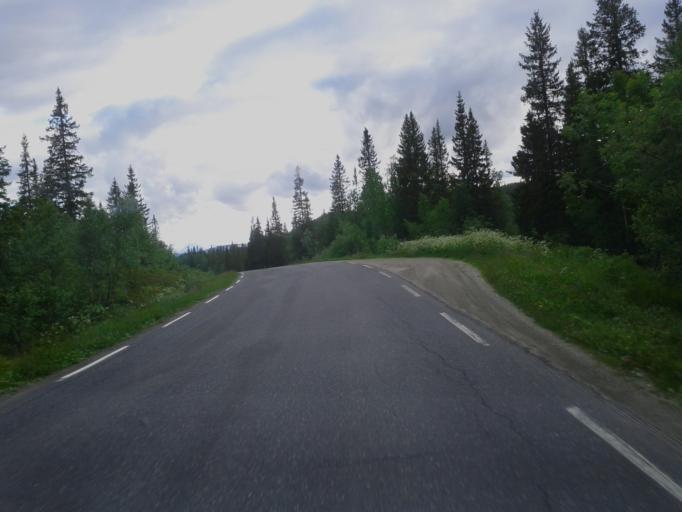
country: NO
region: Nordland
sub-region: Hattfjelldal
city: Hattfjelldal
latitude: 65.5577
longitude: 13.7522
